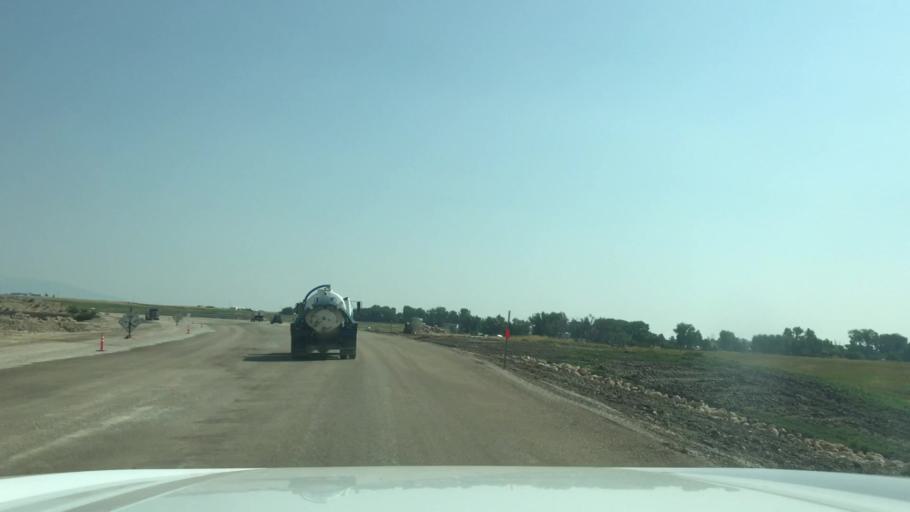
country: US
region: Montana
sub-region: Judith Basin County
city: Stanford
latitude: 47.0073
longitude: -109.8713
